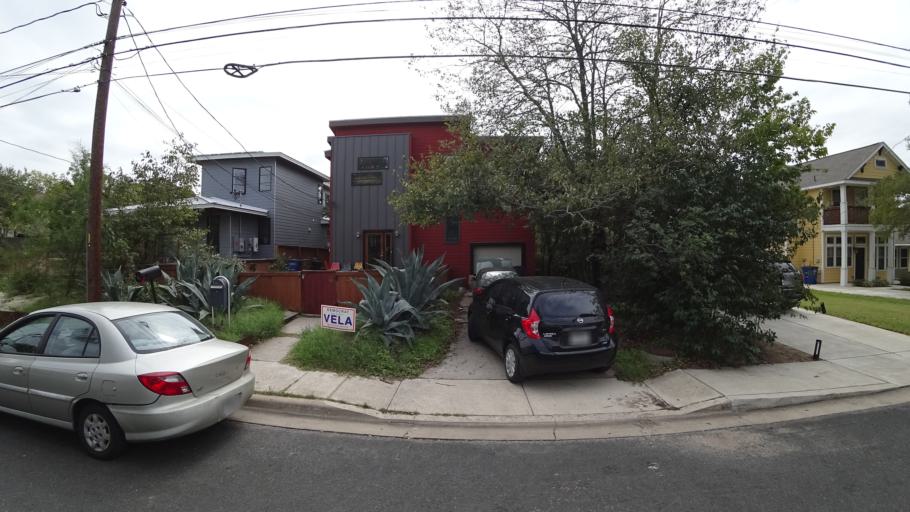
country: US
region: Texas
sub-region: Travis County
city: Austin
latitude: 30.2751
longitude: -97.7184
